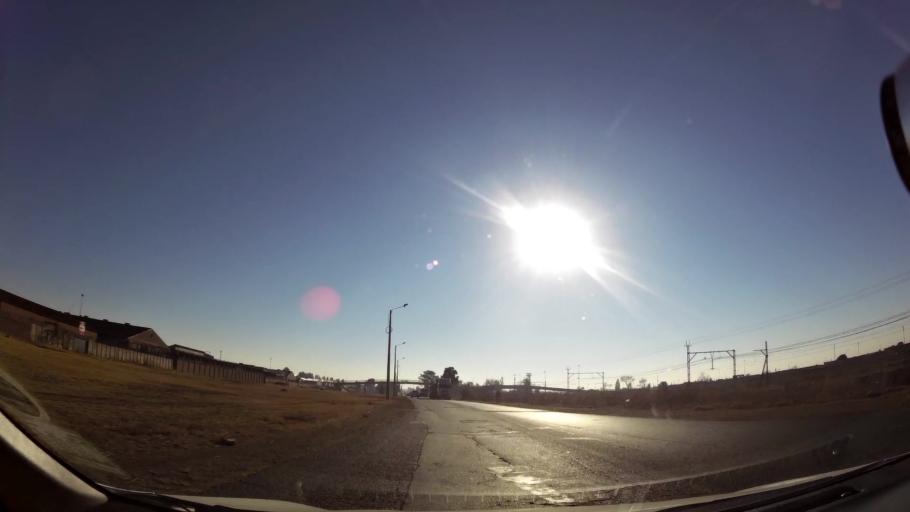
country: ZA
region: Gauteng
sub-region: Ekurhuleni Metropolitan Municipality
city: Germiston
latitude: -26.3523
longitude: 28.1244
